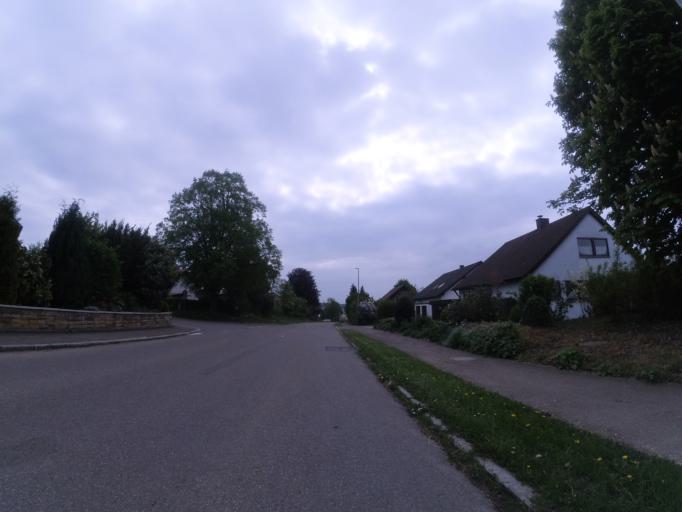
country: DE
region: Baden-Wuerttemberg
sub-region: Tuebingen Region
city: Staig
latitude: 48.3018
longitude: 9.9839
